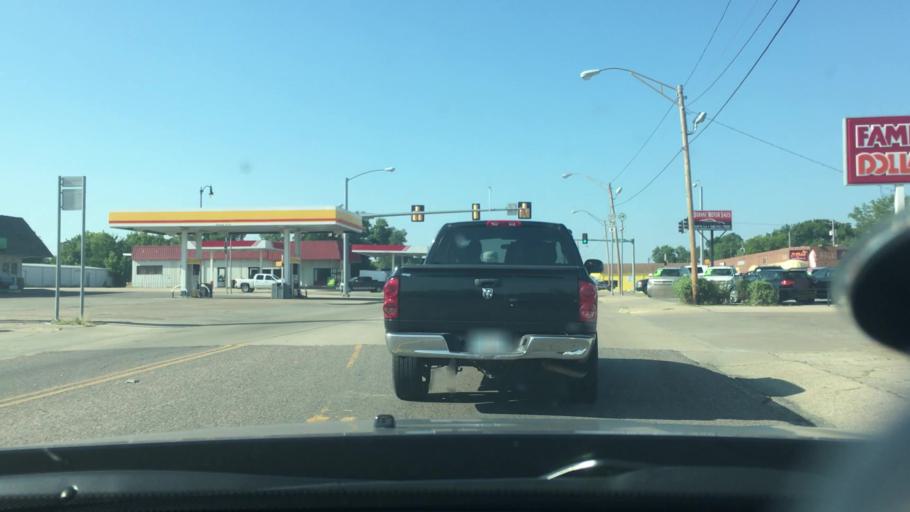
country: US
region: Oklahoma
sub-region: Bryan County
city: Durant
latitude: 33.9985
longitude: -96.3737
